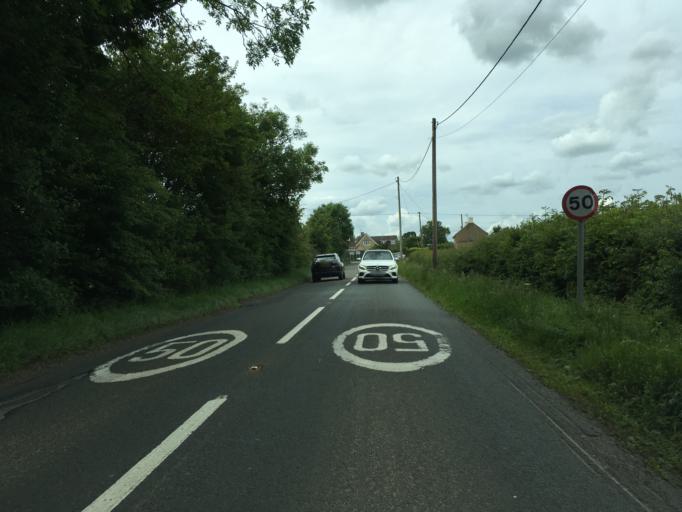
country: GB
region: England
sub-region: Wiltshire
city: Royal Wootton Bassett
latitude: 51.5627
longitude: -1.9488
